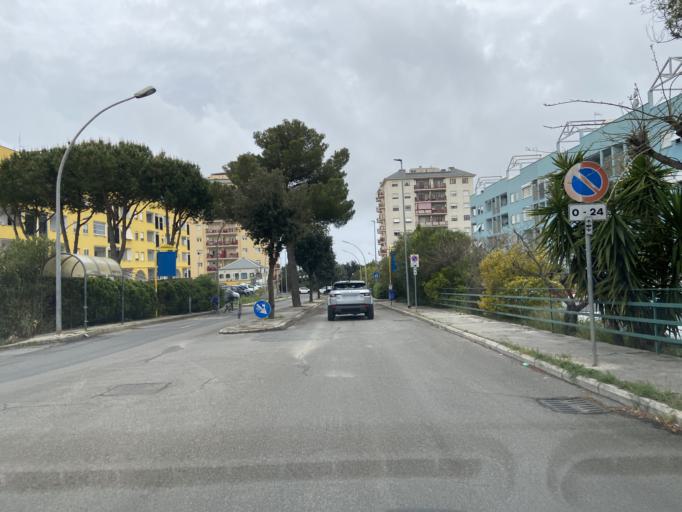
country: IT
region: Latium
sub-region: Citta metropolitana di Roma Capitale
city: Civitavecchia
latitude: 42.0985
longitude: 11.8227
